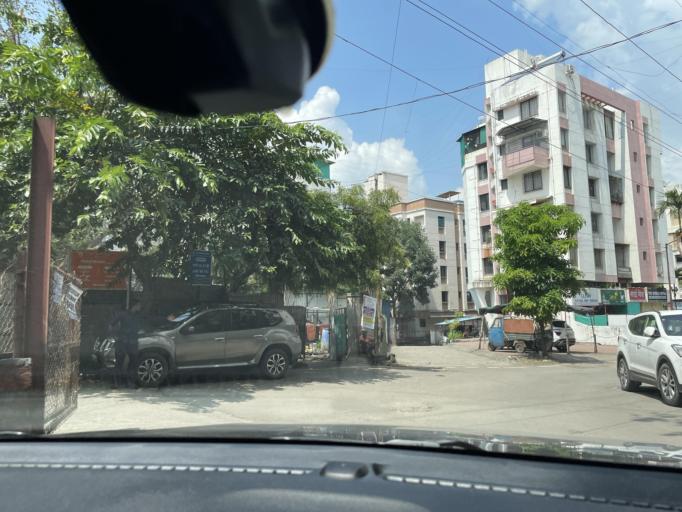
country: IN
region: Maharashtra
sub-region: Pune Division
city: Kharakvasla
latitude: 18.5106
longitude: 73.7787
